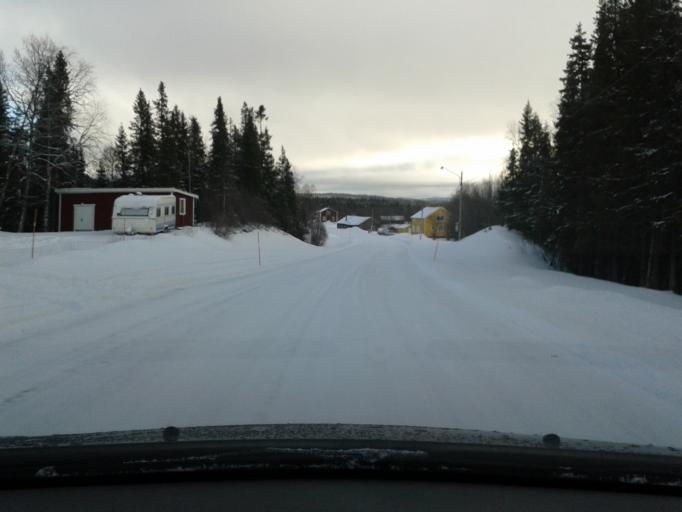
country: SE
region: Vaesterbotten
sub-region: Vilhelmina Kommun
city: Sjoberg
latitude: 65.2512
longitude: 15.5740
